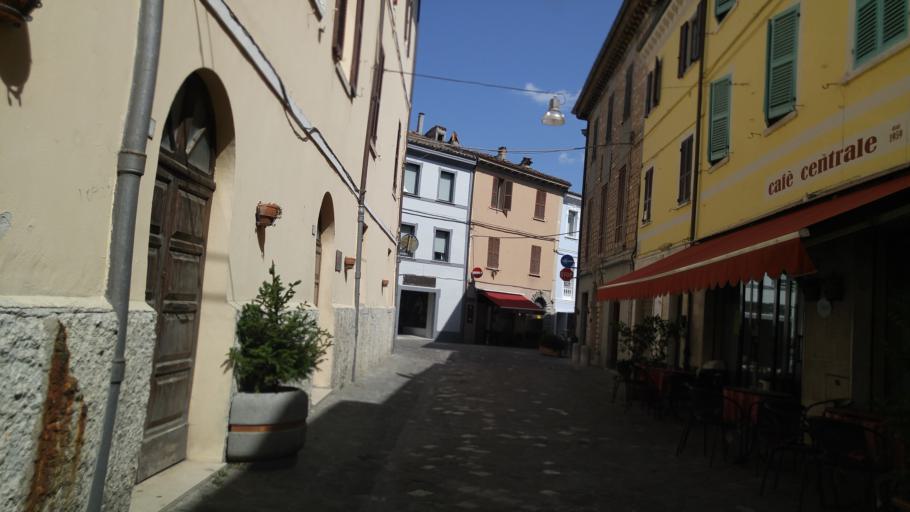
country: IT
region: The Marches
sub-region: Provincia di Pesaro e Urbino
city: Acqualagna
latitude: 43.6167
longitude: 12.6716
